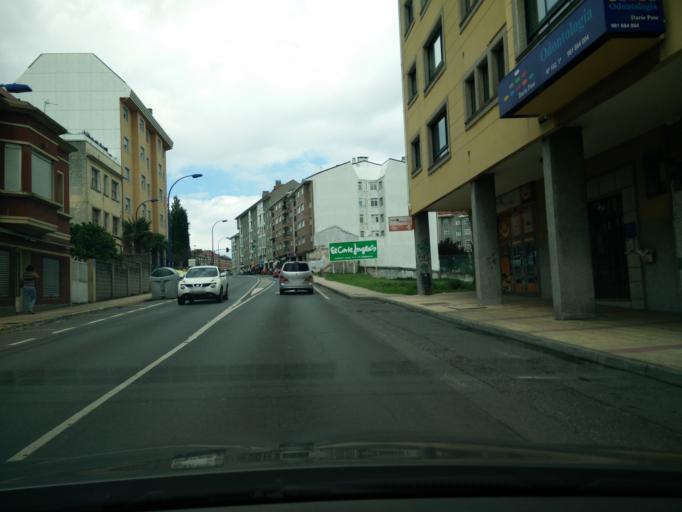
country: ES
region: Galicia
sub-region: Provincia da Coruna
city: Culleredo
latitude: 43.3163
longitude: -8.3835
